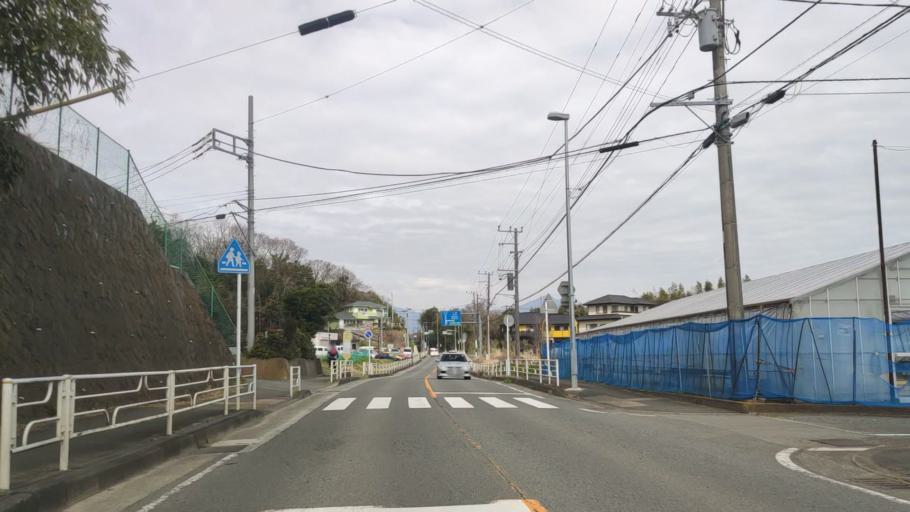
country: JP
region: Kanagawa
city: Ninomiya
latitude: 35.3086
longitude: 139.2258
